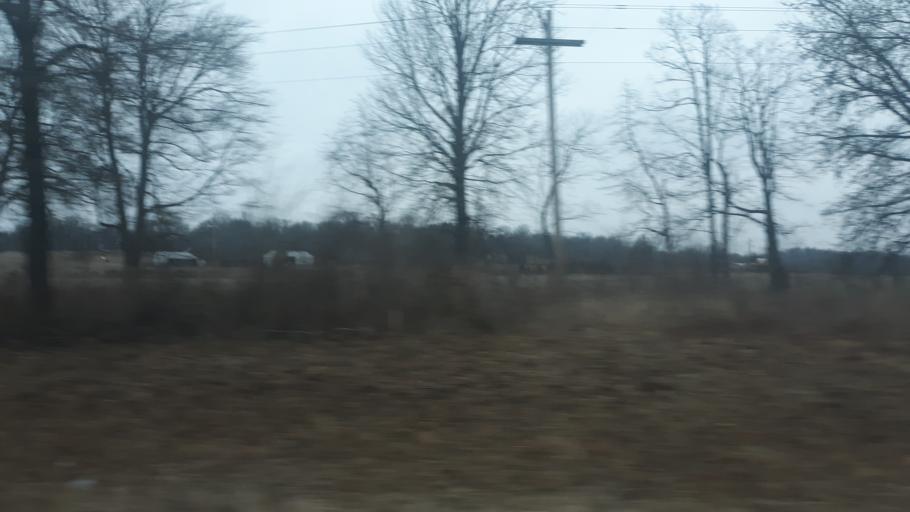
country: US
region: Illinois
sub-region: White County
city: Norris City
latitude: 38.0188
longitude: -88.2715
